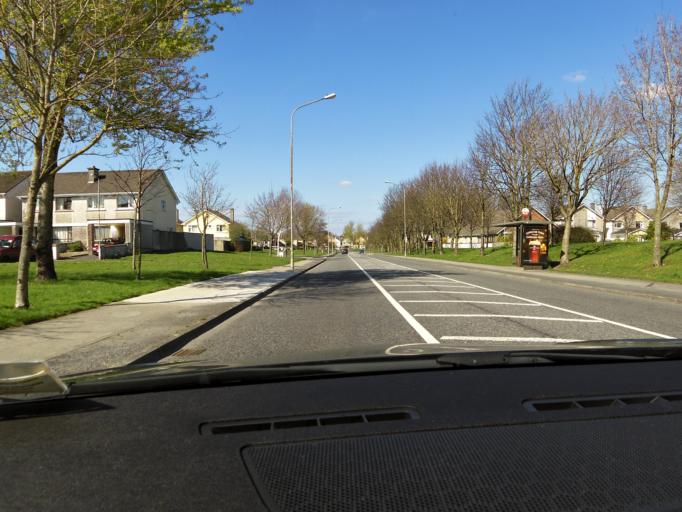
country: IE
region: Connaught
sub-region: County Galway
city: Gaillimh
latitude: 53.2843
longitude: -9.0734
